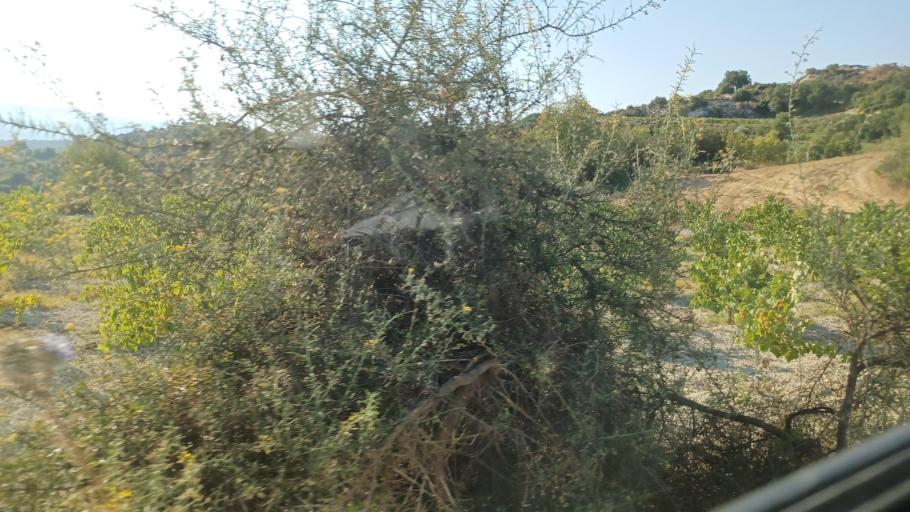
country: CY
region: Pafos
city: Mesogi
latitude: 34.8849
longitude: 32.5198
